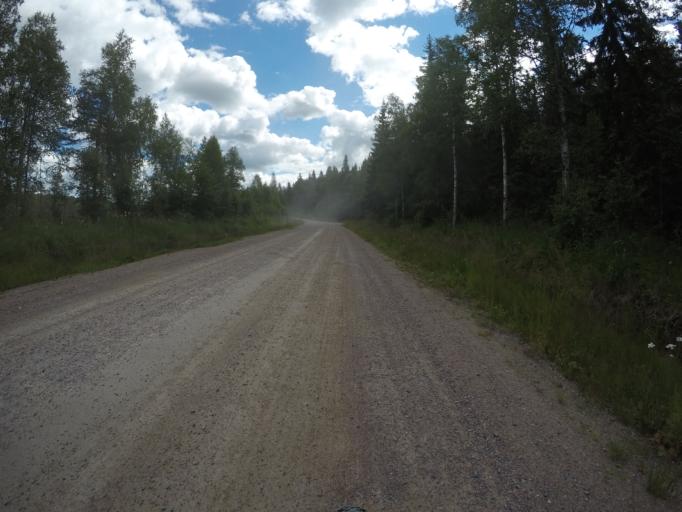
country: SE
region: Vaermland
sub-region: Filipstads Kommun
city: Lesjofors
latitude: 60.1344
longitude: 14.4064
